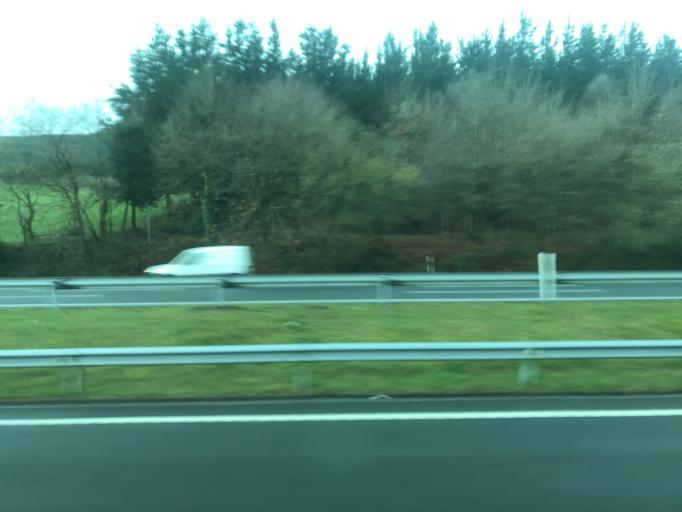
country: ES
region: Basque Country
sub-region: Bizkaia
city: Elexalde
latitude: 43.1236
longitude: -2.9174
